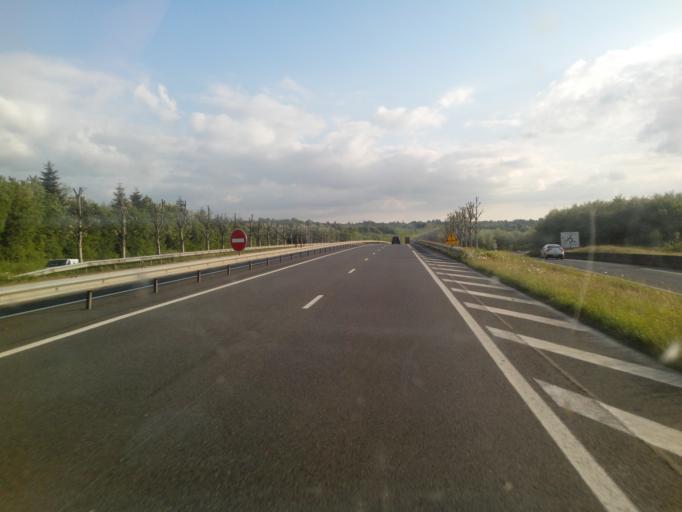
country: FR
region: Lower Normandy
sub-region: Departement du Calvados
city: Saint-Martin-des-Besaces
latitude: 49.0270
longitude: -0.8310
